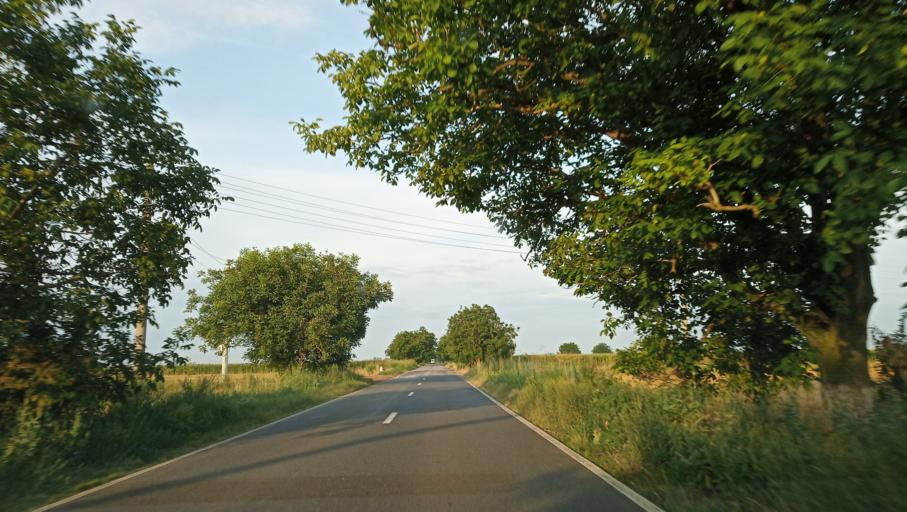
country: RO
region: Giurgiu
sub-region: Comuna Greaca
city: Greaca
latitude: 44.1035
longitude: 26.2919
